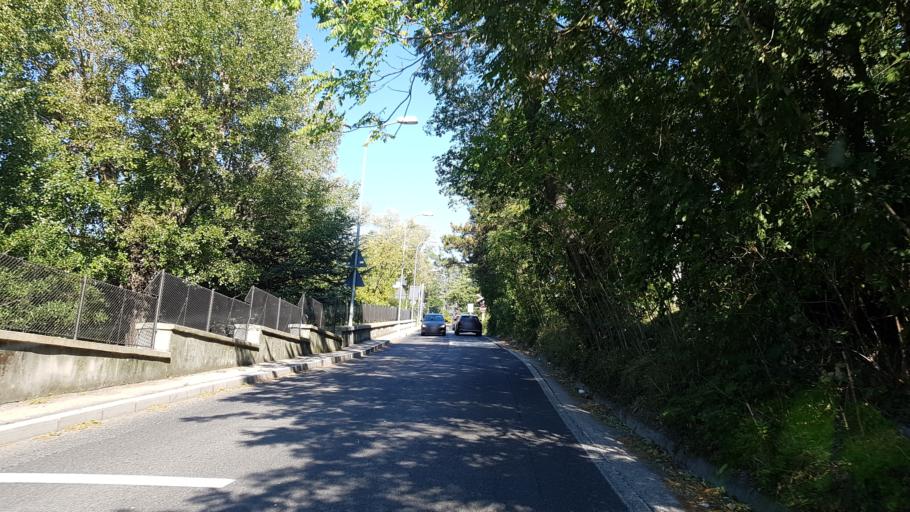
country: IT
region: Friuli Venezia Giulia
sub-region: Provincia di Trieste
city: Trieste
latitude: 45.6654
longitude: 13.7867
